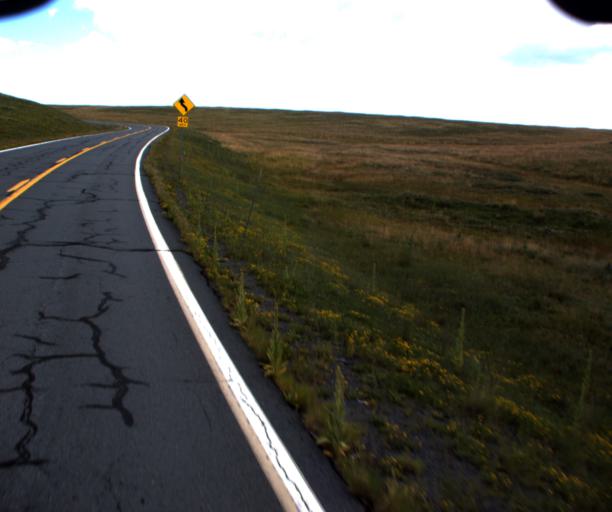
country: US
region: Arizona
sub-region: Apache County
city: Eagar
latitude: 33.9559
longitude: -109.3953
